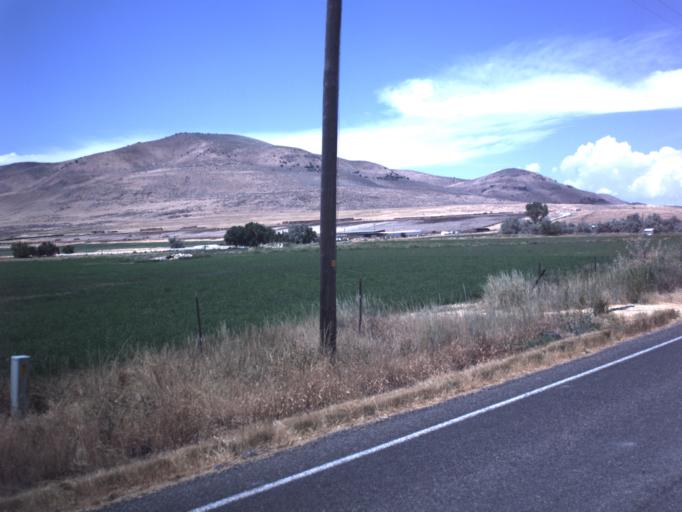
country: US
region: Utah
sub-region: Box Elder County
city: Tremonton
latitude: 41.6548
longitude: -112.2959
